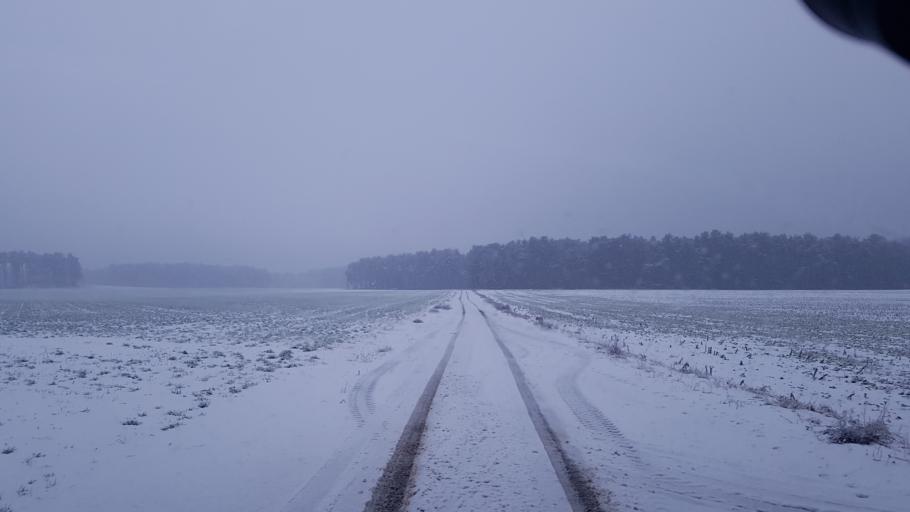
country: DE
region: Brandenburg
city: Schenkendobern
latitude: 51.9032
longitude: 14.5811
